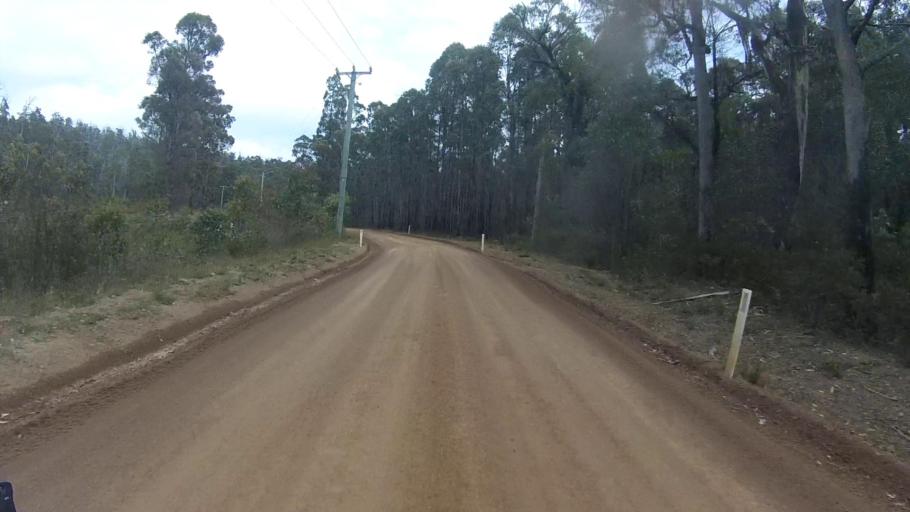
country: AU
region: Tasmania
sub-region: Sorell
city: Sorell
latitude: -42.7482
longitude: 147.7877
